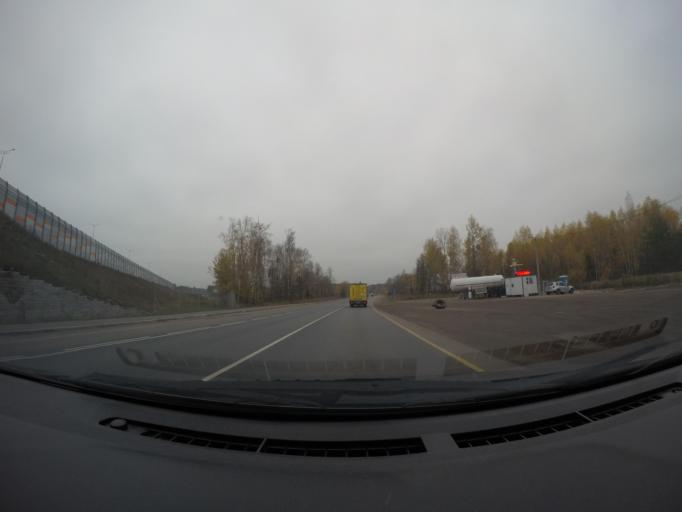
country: RU
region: Moskovskaya
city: Malyshevo
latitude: 55.5358
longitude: 38.4043
